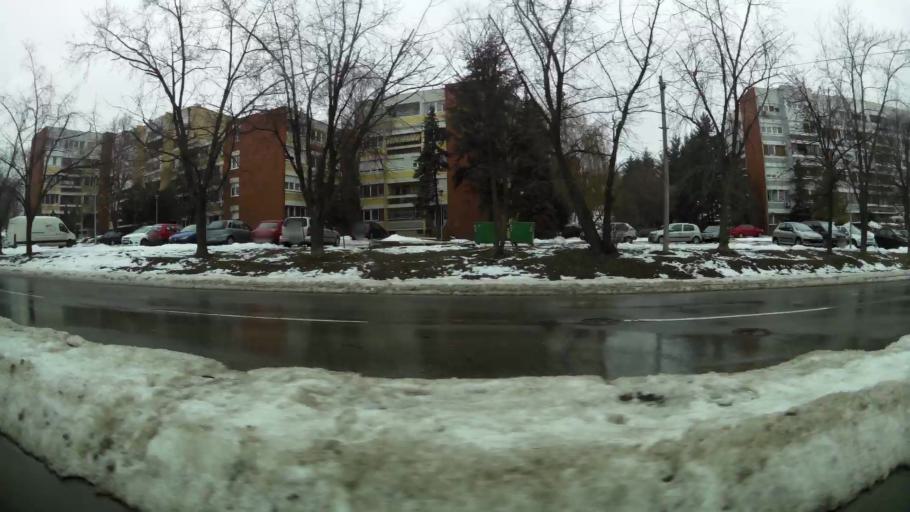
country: RS
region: Central Serbia
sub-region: Belgrade
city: Zvezdara
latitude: 44.7522
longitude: 20.5024
